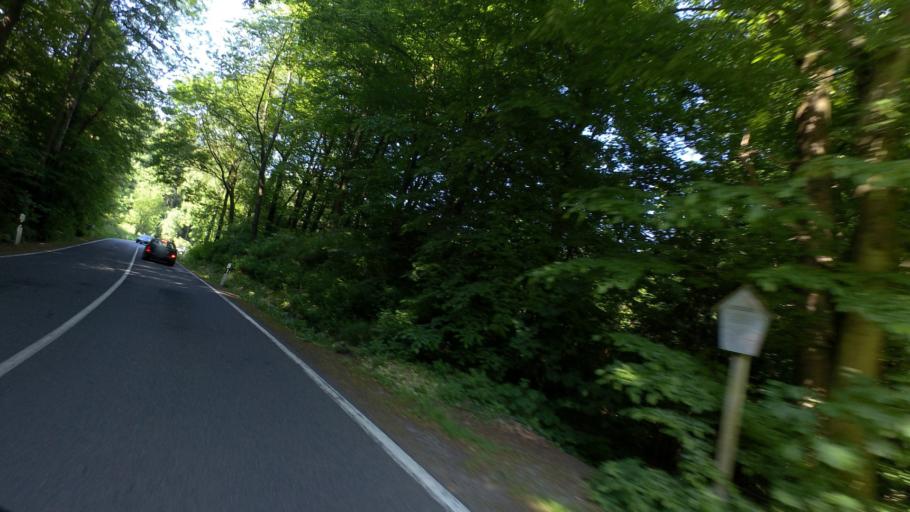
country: DE
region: Saxony
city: Hohnstein
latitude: 50.9827
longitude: 14.1071
